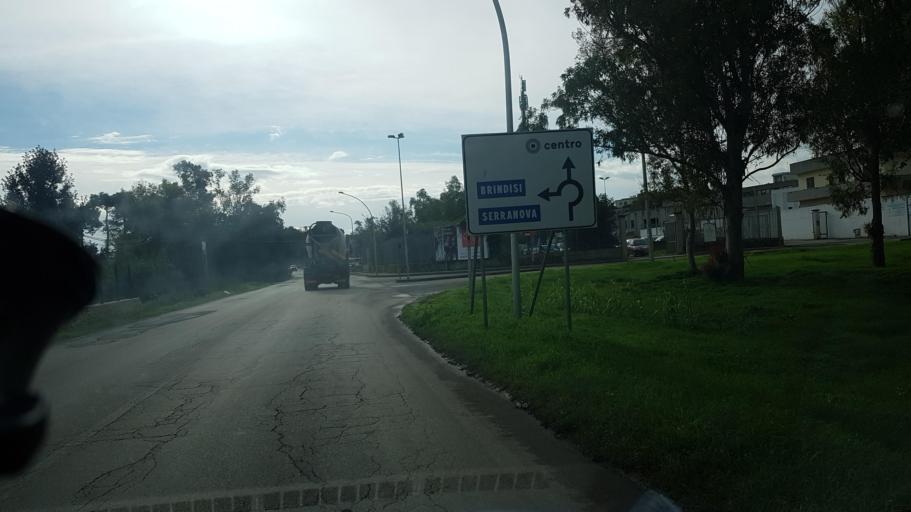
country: IT
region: Apulia
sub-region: Provincia di Brindisi
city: San Vito dei Normanni
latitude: 40.6648
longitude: 17.7055
